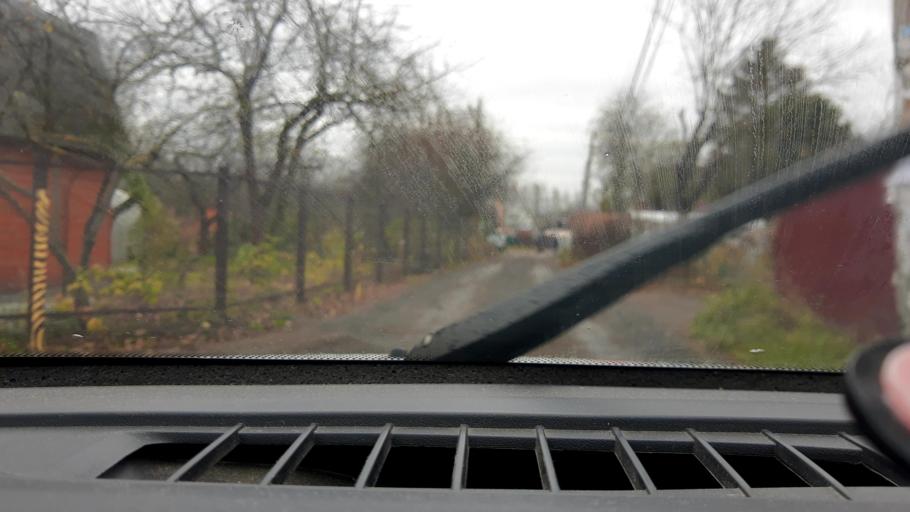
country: RU
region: Nizjnij Novgorod
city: Gorbatovka
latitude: 56.3833
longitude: 43.8120
